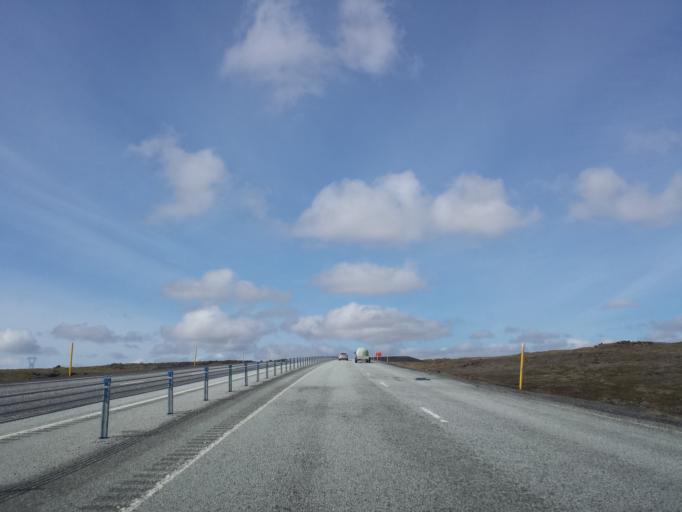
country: IS
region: South
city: Hveragerdi
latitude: 64.0115
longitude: -21.2510
